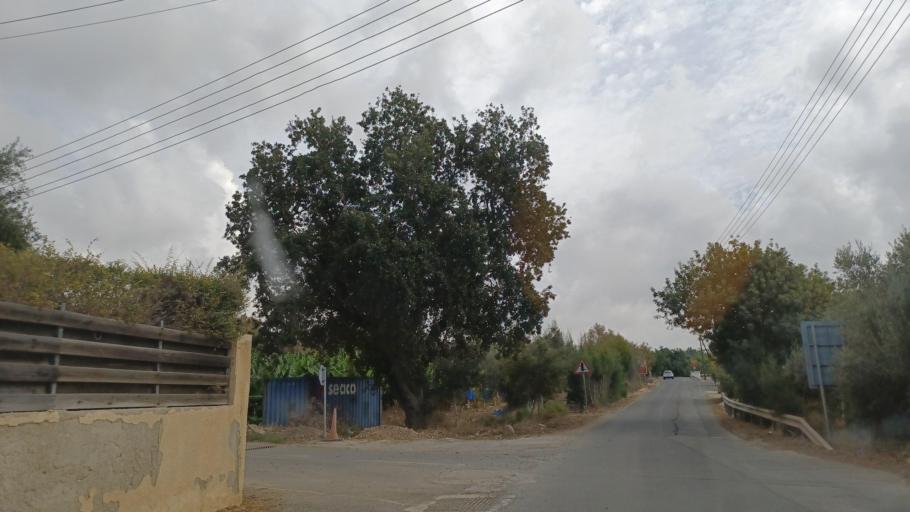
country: CY
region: Pafos
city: Kissonerga
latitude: 34.8295
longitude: 32.4081
